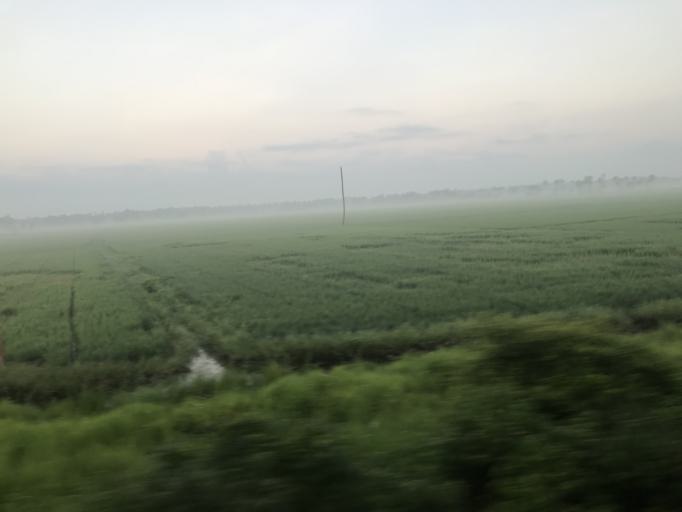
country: IN
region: Andhra Pradesh
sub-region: Guntur
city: Ponnur
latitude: 16.0895
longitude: 80.5672
